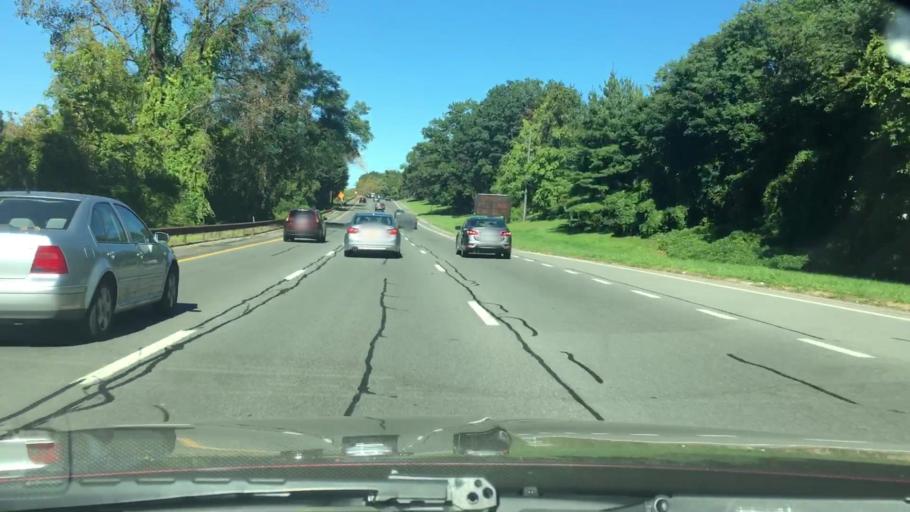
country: US
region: New York
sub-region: Westchester County
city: Tuckahoe
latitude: 40.9571
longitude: -73.8512
